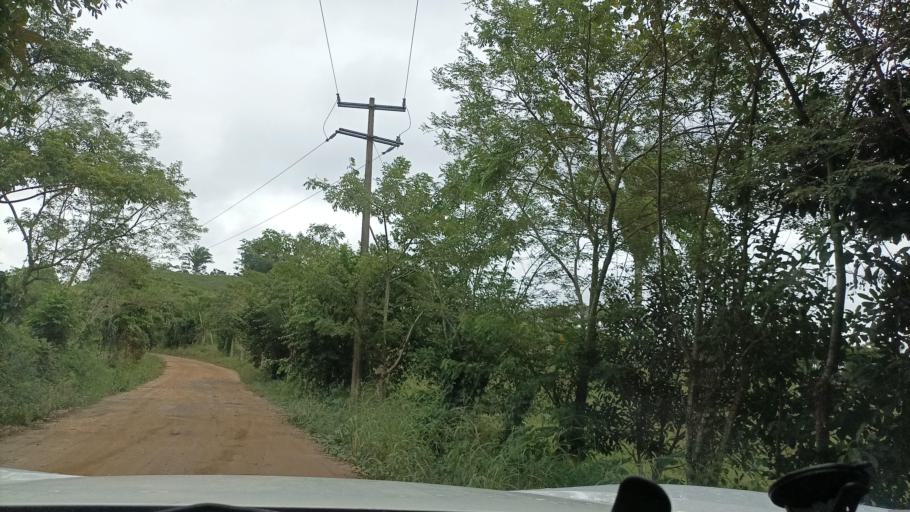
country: MX
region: Veracruz
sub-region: Moloacan
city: Cuichapa
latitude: 17.7959
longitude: -94.3800
